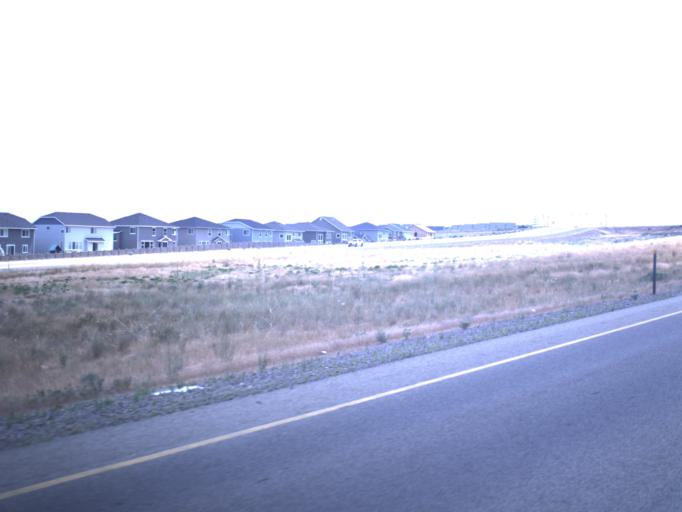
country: US
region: Utah
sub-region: Salt Lake County
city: Herriman
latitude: 40.4924
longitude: -112.0036
